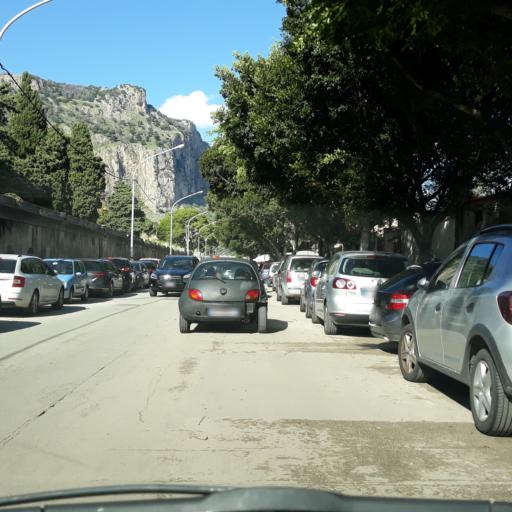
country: IT
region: Sicily
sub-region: Palermo
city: Palermo
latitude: 38.1605
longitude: 13.3713
